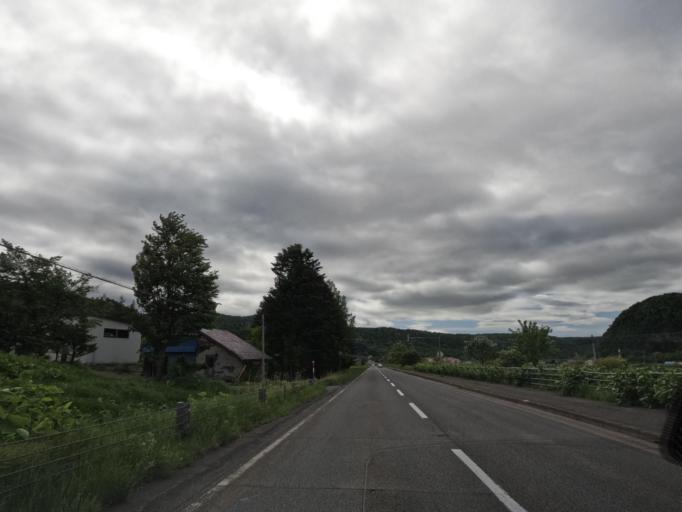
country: JP
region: Hokkaido
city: Kamikawa
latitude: 43.8435
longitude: 142.7246
